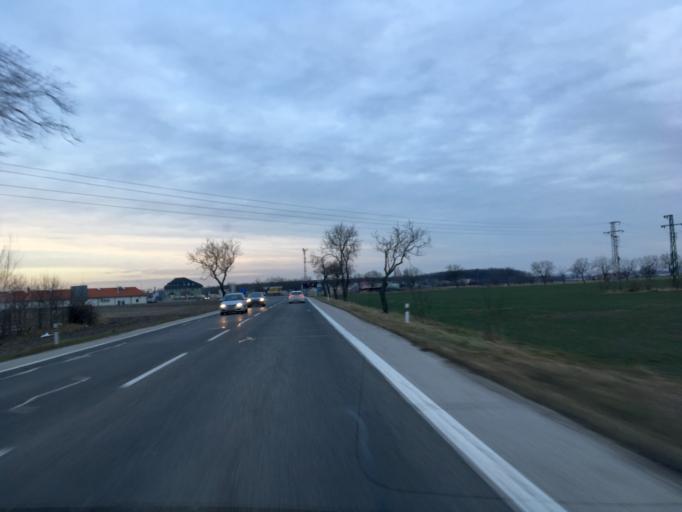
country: SK
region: Trnavsky
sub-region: Okres Dunajska Streda
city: Velky Meder
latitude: 47.8665
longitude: 17.7575
